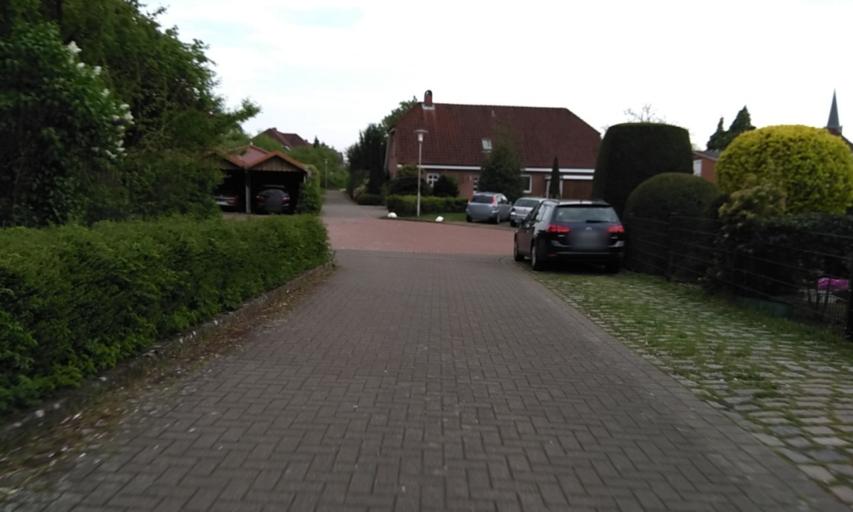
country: DE
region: Lower Saxony
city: Harsefeld
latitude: 53.4561
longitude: 9.5050
